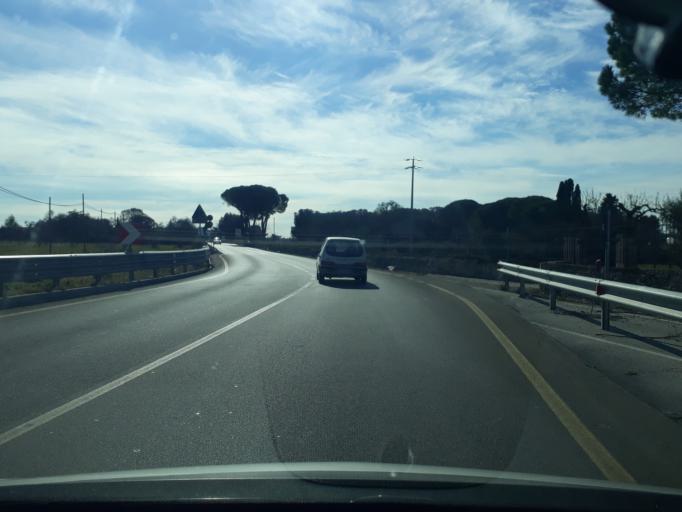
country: IT
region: Apulia
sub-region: Provincia di Bari
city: Locorotondo
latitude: 40.7354
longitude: 17.3326
